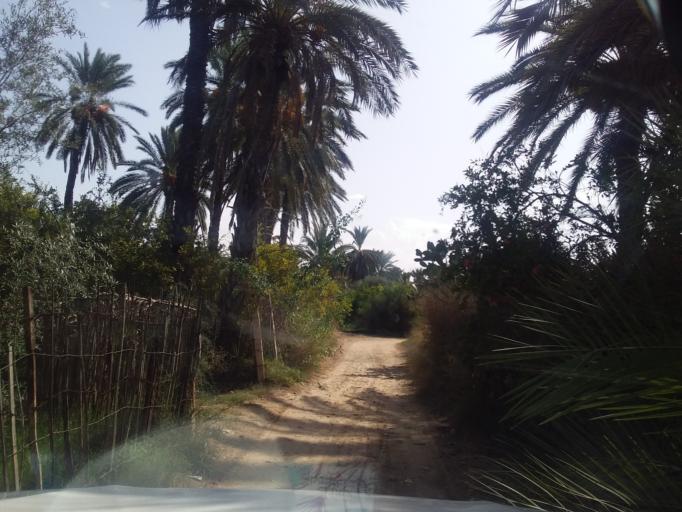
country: TN
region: Qabis
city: Gabes
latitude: 33.6262
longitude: 10.2882
